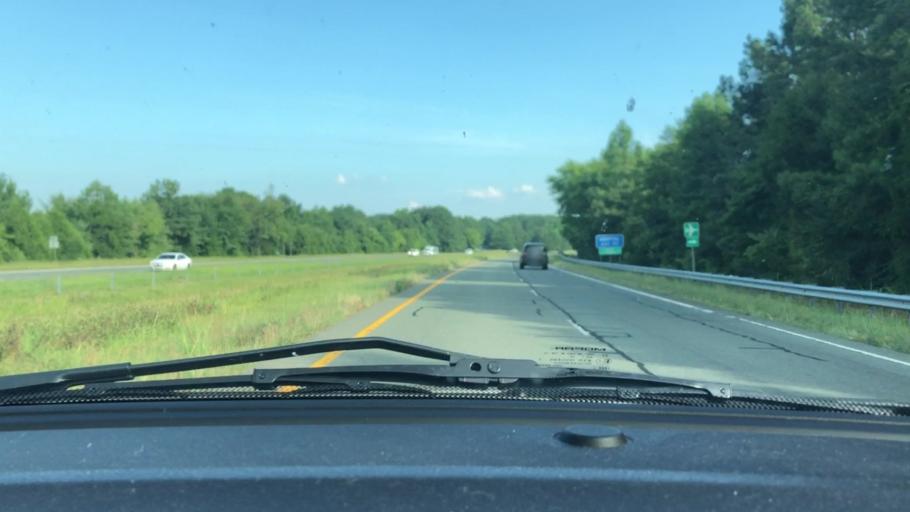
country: US
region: North Carolina
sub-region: Chatham County
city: Siler City
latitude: 35.7406
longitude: -79.4352
